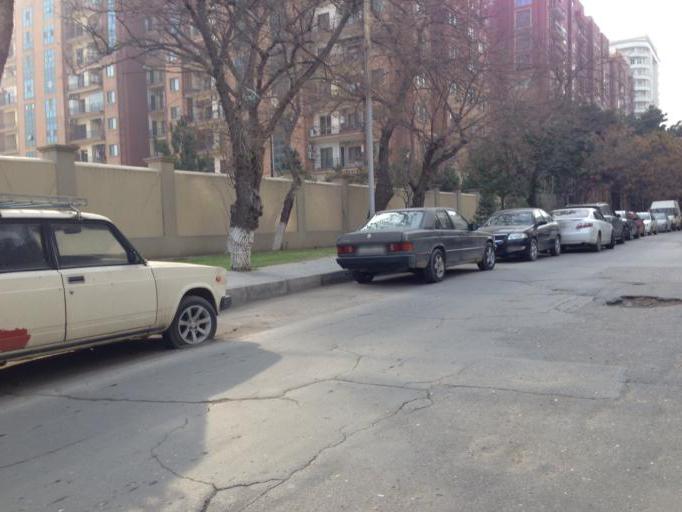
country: AZ
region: Baki
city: Baku
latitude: 40.4004
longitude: 49.8619
